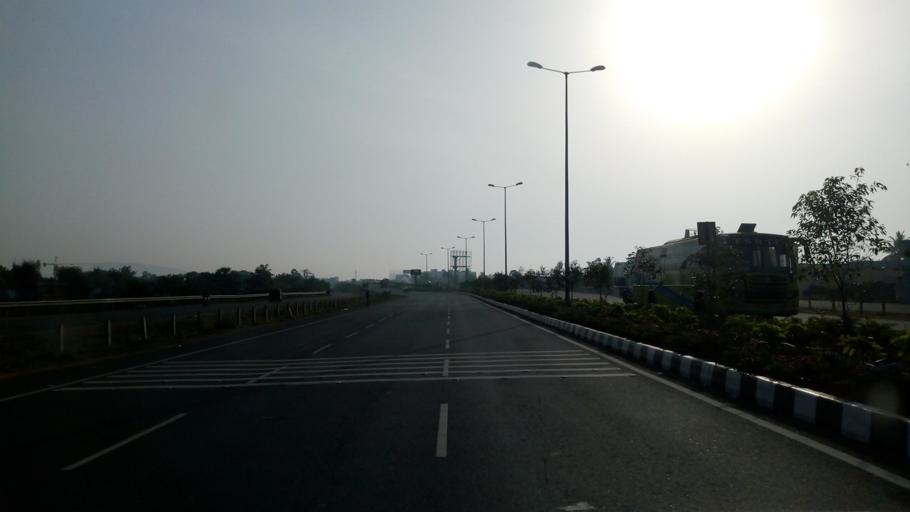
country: IN
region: Andhra Pradesh
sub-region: Guntur
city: Mangalagiri
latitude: 16.3919
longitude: 80.5406
